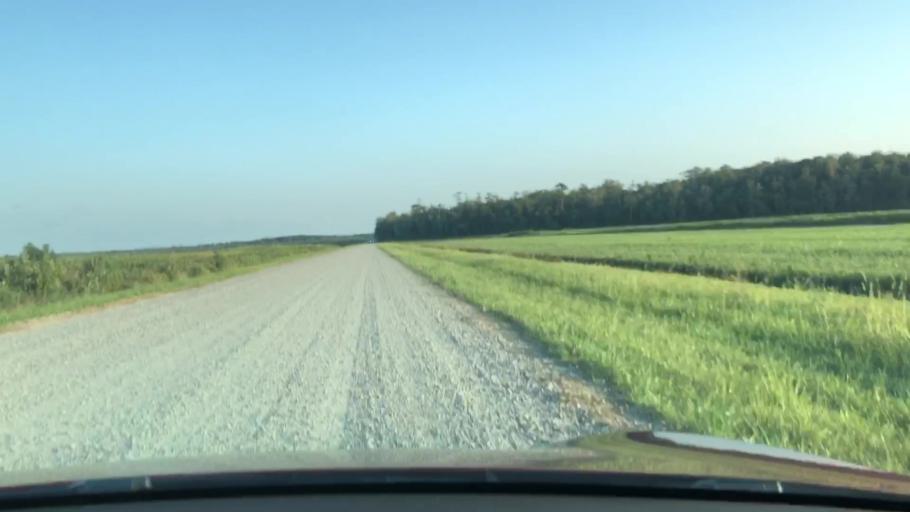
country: US
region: North Carolina
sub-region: Dare County
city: Manteo
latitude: 35.8481
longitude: -75.8611
